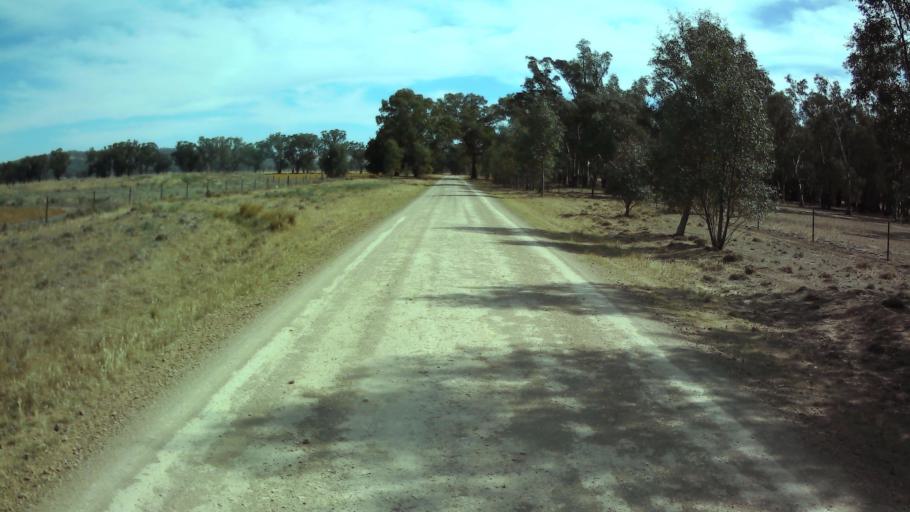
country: AU
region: New South Wales
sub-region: Weddin
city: Grenfell
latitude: -33.7035
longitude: 148.3017
